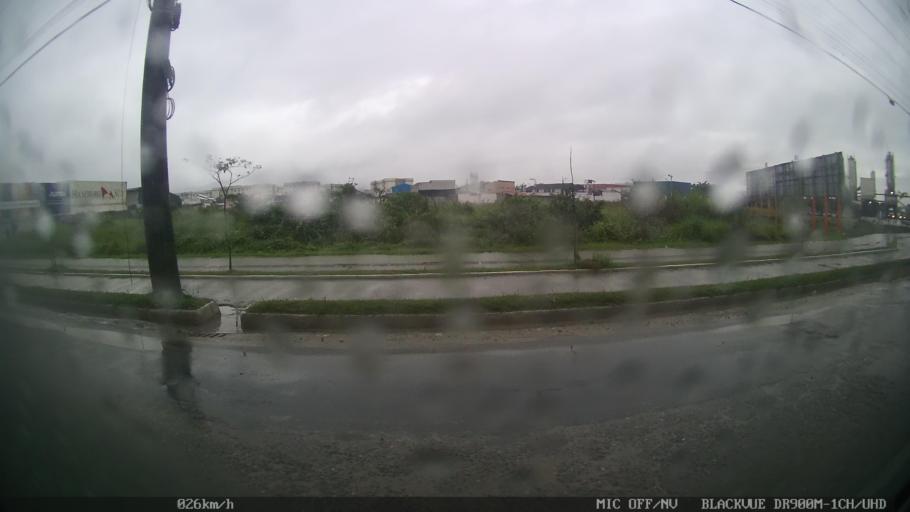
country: BR
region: Santa Catarina
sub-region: Itajai
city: Itajai
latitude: -26.9173
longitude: -48.7053
